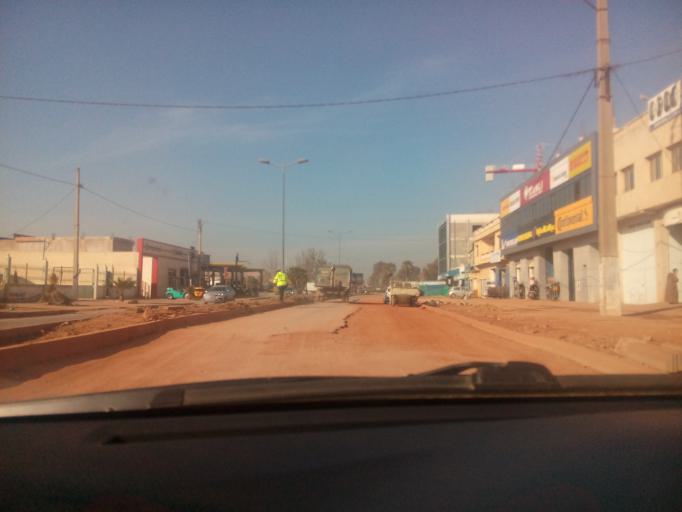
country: DZ
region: Oran
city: Es Senia
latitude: 35.6476
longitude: -0.6108
